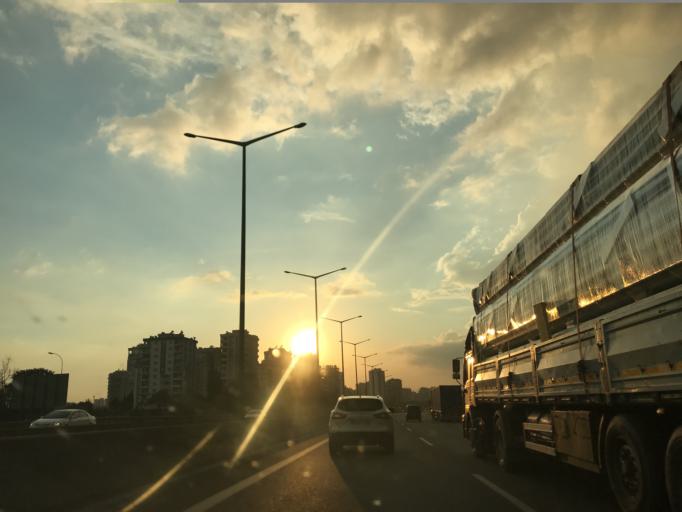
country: TR
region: Adana
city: Seyhan
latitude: 37.0309
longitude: 35.2818
